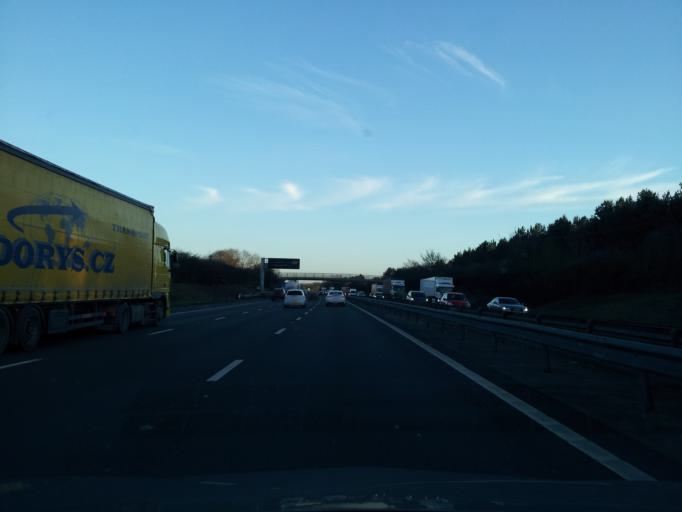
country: GB
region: England
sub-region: Milton Keynes
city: Newport Pagnell
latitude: 52.0672
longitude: -0.7188
